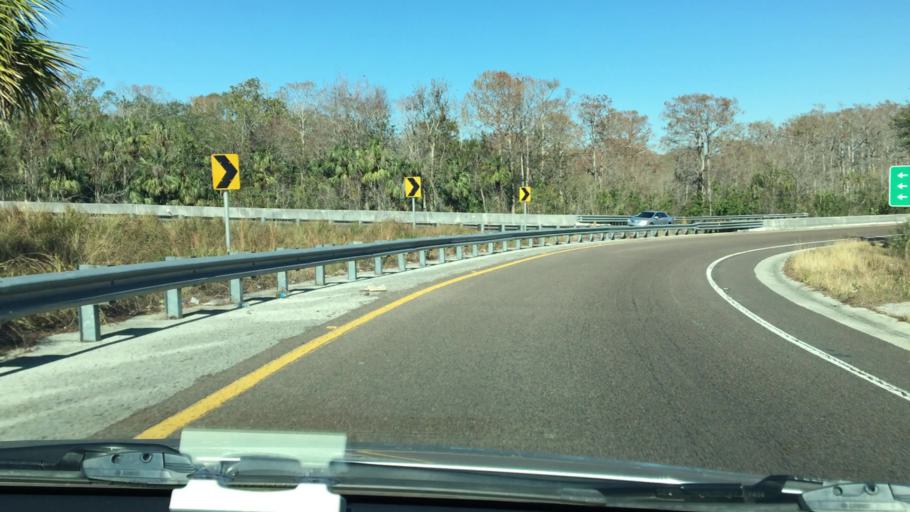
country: US
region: Florida
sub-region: Volusia County
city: DeBary
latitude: 28.8323
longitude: -81.3246
